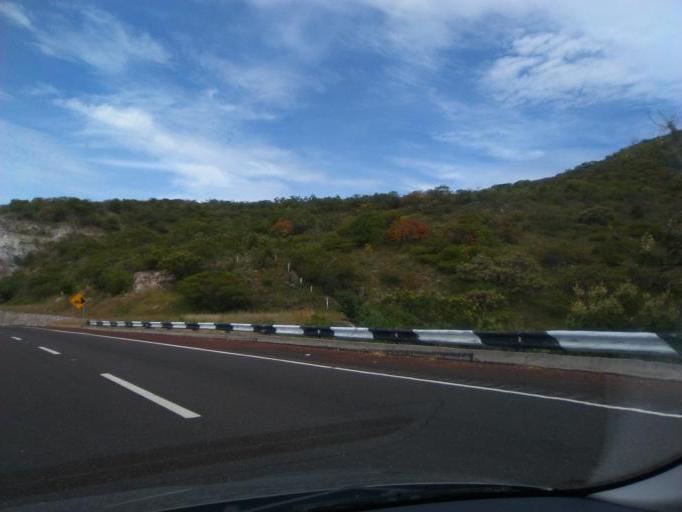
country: MX
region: Guerrero
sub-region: Eduardo Neri
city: Tlanipatla
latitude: 17.8689
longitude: -99.4004
